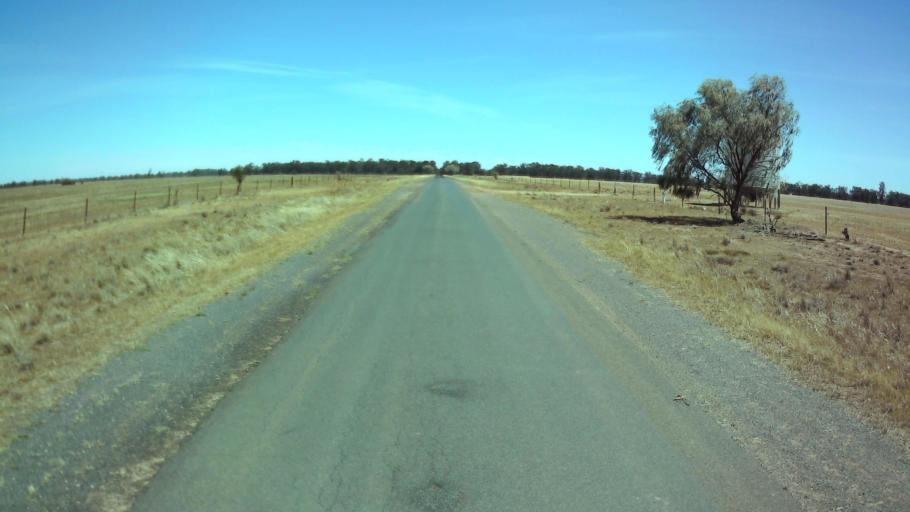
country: AU
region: New South Wales
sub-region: Weddin
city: Grenfell
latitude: -33.8593
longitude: 147.6937
